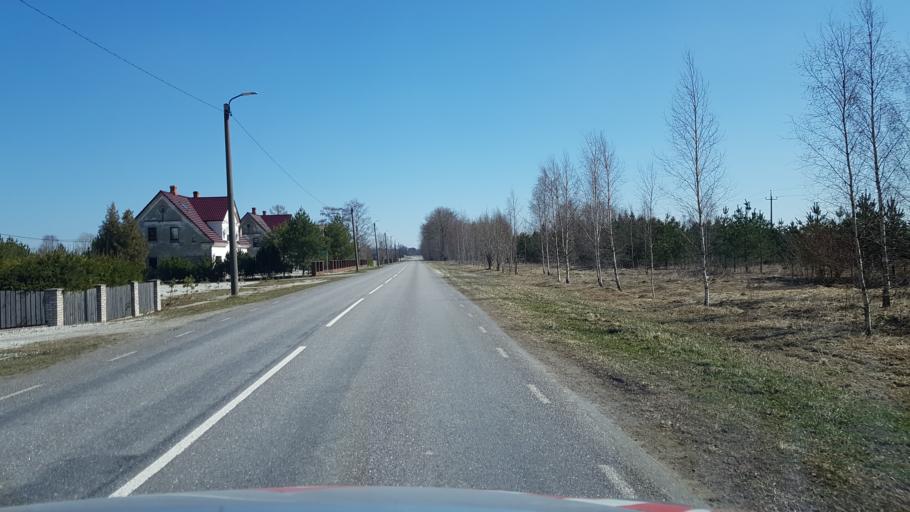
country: EE
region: Ida-Virumaa
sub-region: Kohtla-Nomme vald
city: Kohtla-Nomme
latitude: 59.3555
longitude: 27.2171
